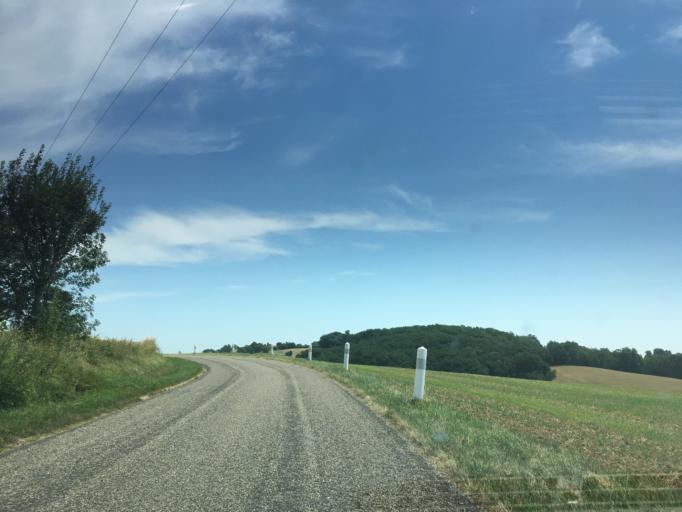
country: FR
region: Midi-Pyrenees
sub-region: Departement du Gers
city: Jegun
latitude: 43.8113
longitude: 0.5140
